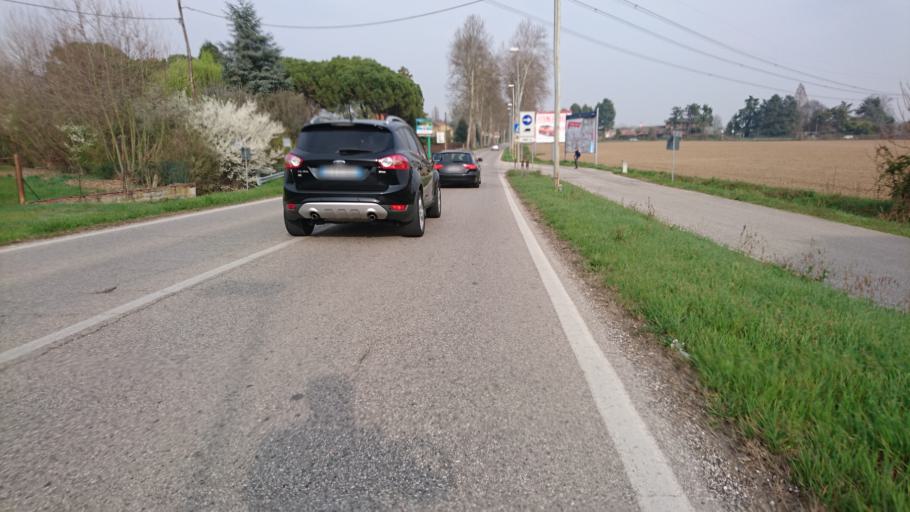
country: IT
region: Veneto
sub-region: Provincia di Padova
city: Mandriola-Sant'Agostino
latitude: 45.3659
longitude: 11.8212
